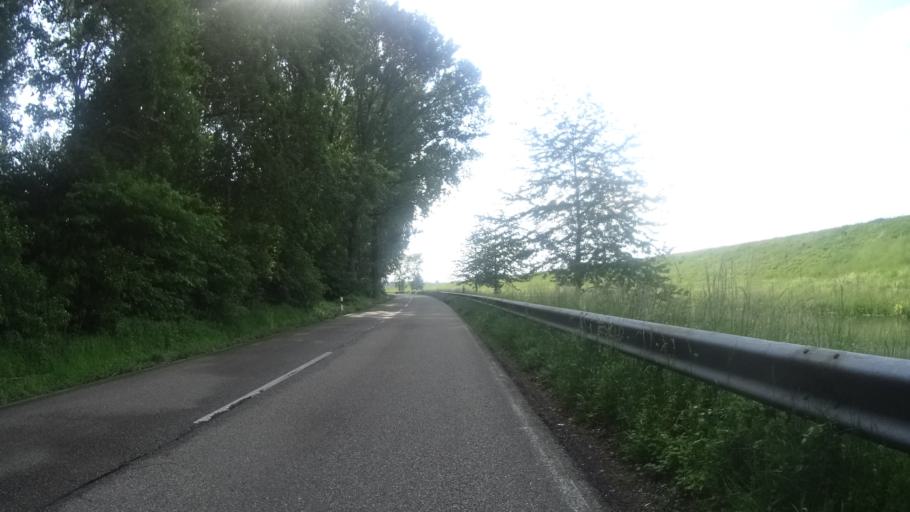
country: DE
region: Baden-Wuerttemberg
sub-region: Karlsruhe Region
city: Schwarzach
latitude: 48.7889
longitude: 8.0477
